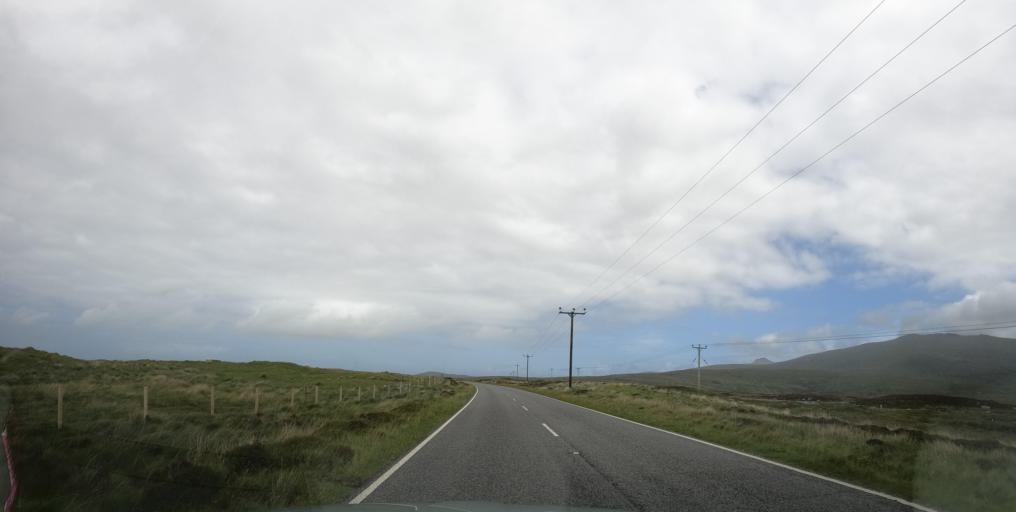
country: GB
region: Scotland
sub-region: Eilean Siar
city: Isle of South Uist
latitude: 57.2518
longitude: -7.3768
